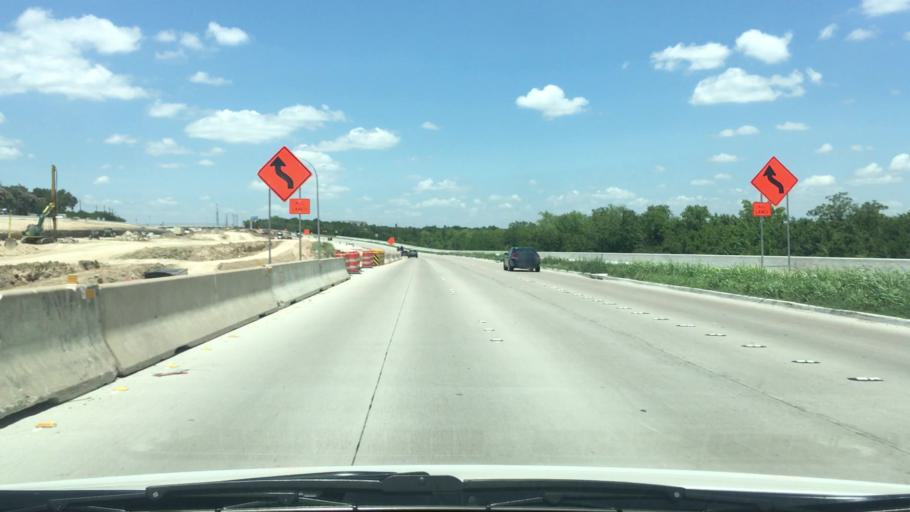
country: US
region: Texas
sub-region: Travis County
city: Austin
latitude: 30.3032
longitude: -97.6603
